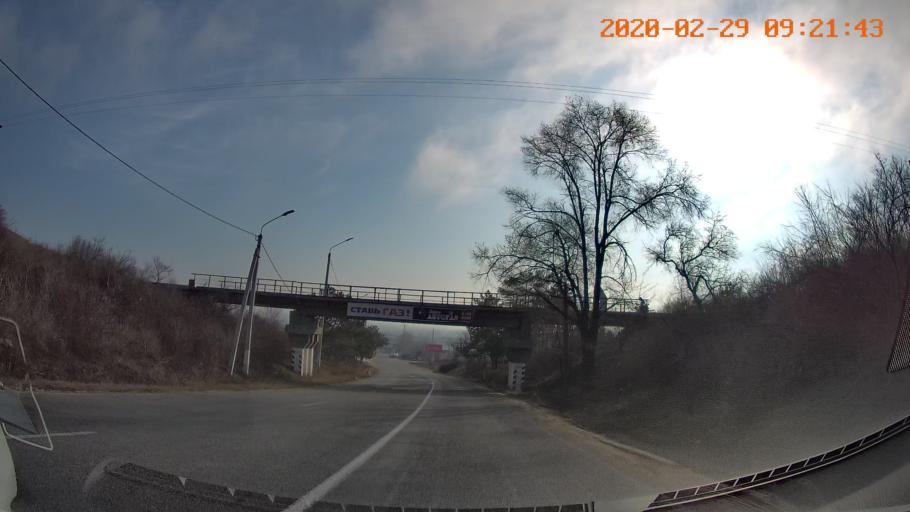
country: MD
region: Telenesti
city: Pervomaisc
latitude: 46.7381
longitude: 29.9623
